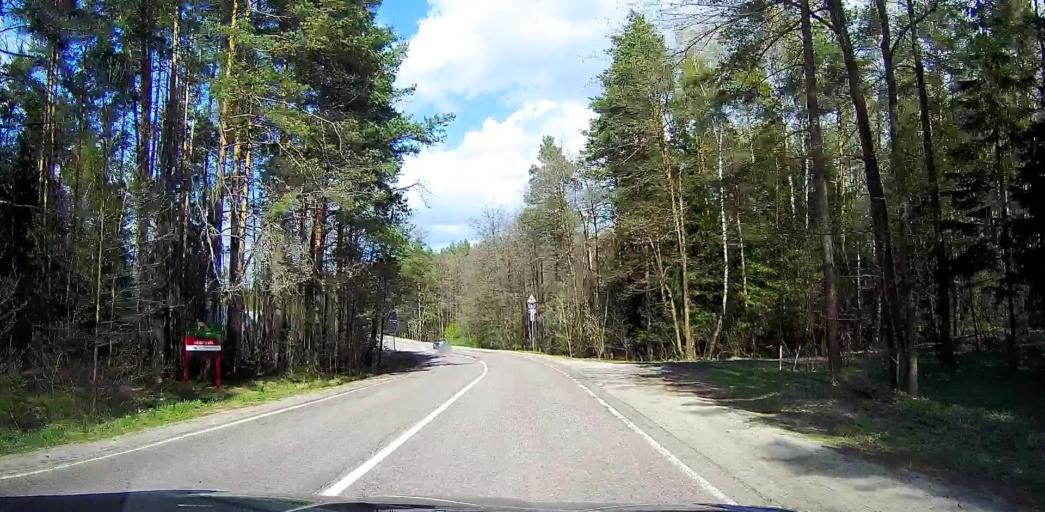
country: RU
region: Moskovskaya
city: Davydovo
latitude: 55.5689
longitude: 38.8228
